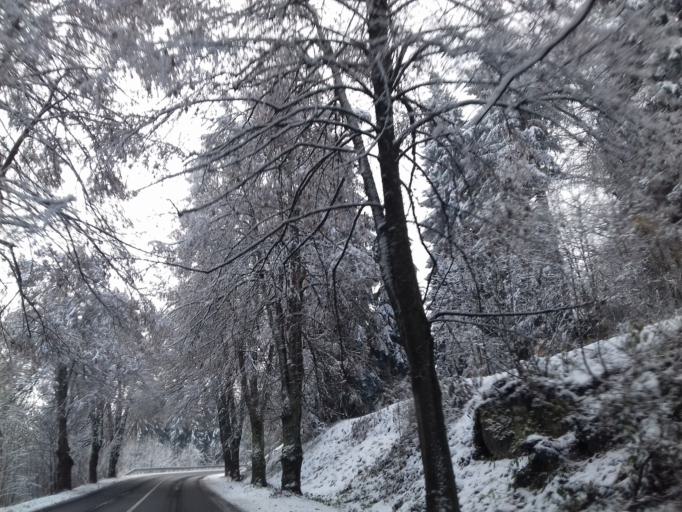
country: CZ
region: Plzensky
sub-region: Okres Domazlice
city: Klenci pod Cerchovem
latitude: 49.4130
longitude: 12.8042
